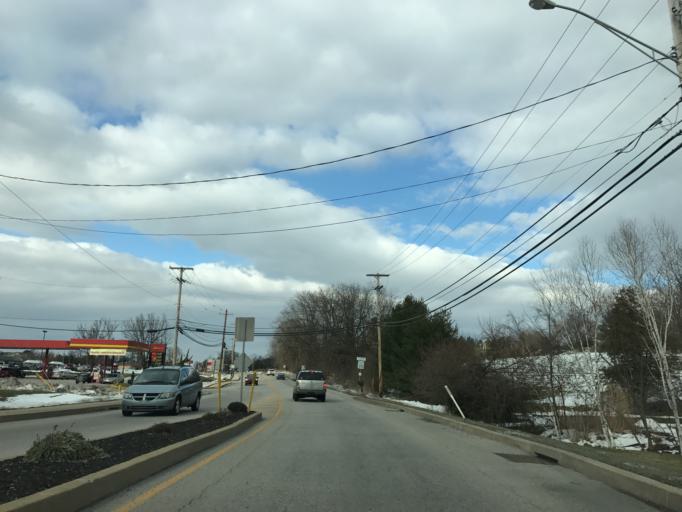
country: US
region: Pennsylvania
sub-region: York County
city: Spring Grove
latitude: 39.8834
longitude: -76.8631
